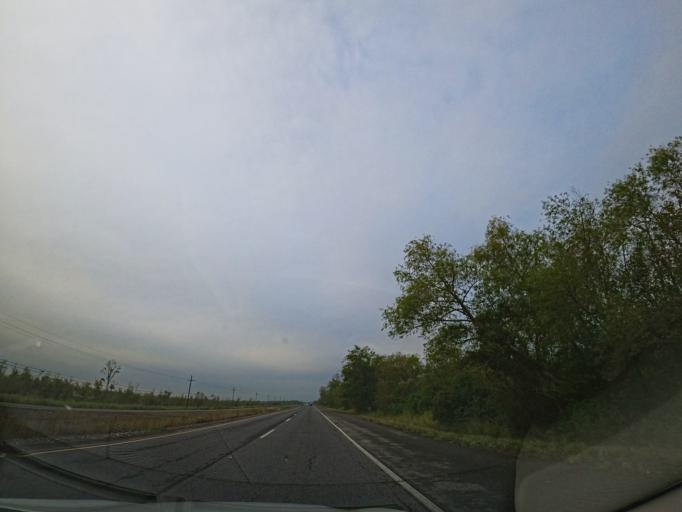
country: US
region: Louisiana
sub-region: Lafourche Parish
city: Raceland
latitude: 29.6747
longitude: -90.6576
